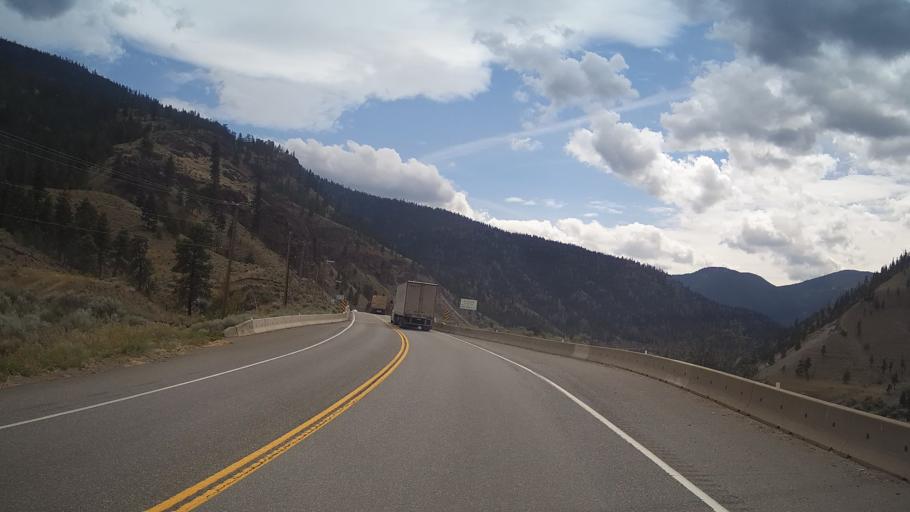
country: CA
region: British Columbia
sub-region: Thompson-Nicola Regional District
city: Ashcroft
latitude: 50.3122
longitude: -121.3962
